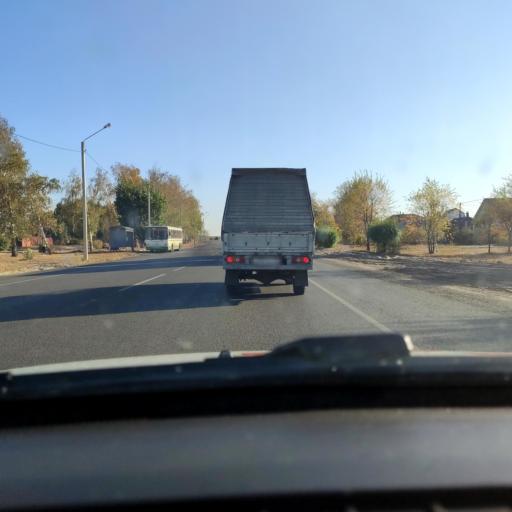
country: RU
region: Voronezj
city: Pridonskoy
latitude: 51.7017
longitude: 39.0776
